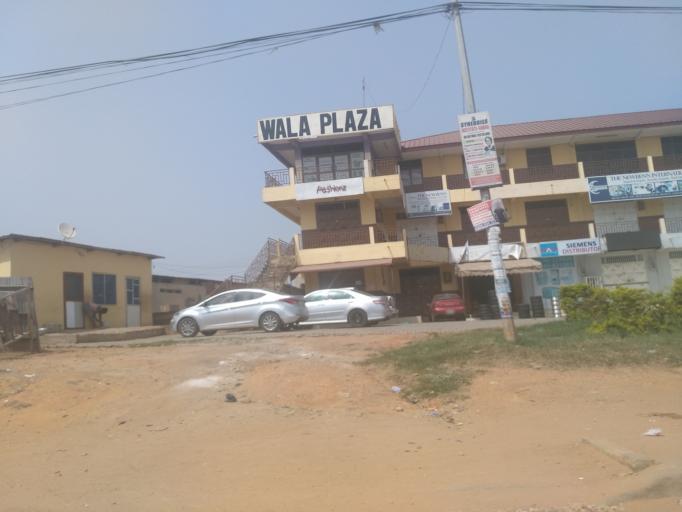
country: GH
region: Greater Accra
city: Dome
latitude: 5.6100
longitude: -0.2365
